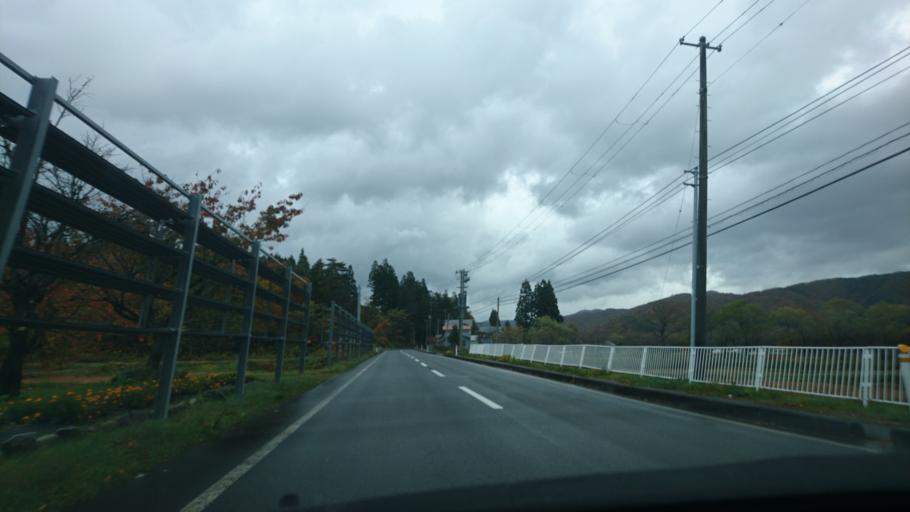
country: JP
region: Akita
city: Kakunodatemachi
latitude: 39.4938
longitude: 140.8130
